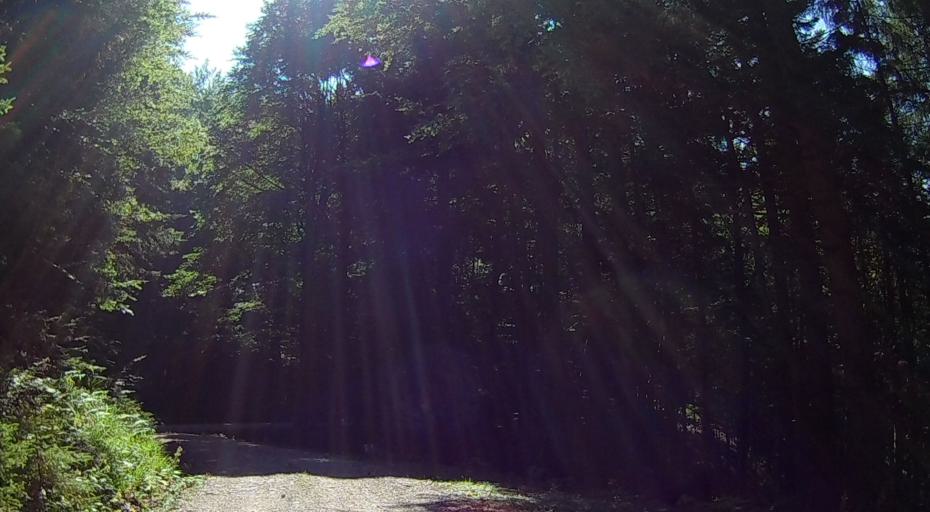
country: SI
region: Selnica ob Dravi
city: Selnica ob Dravi
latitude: 46.4915
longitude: 15.4613
